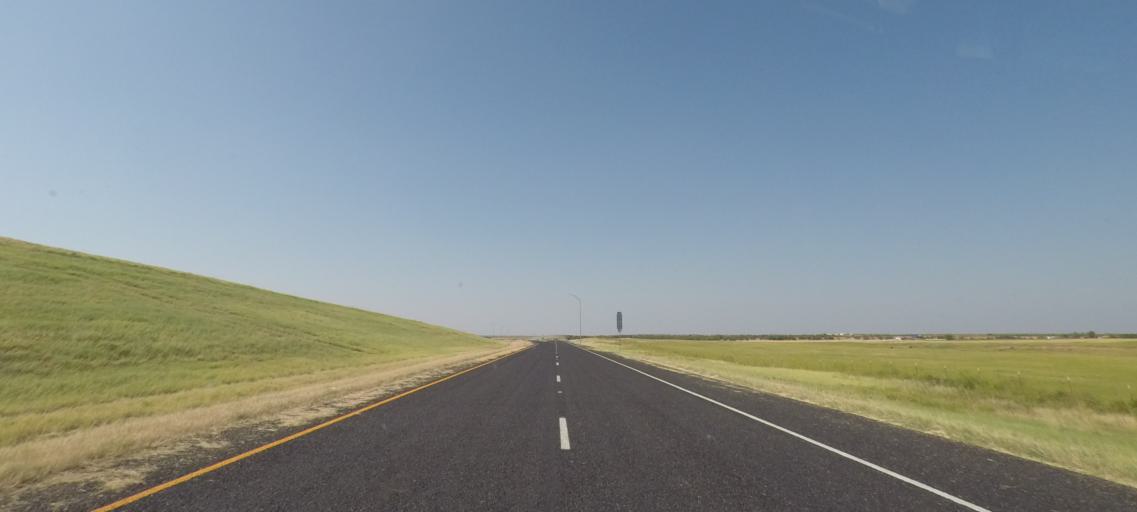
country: US
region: Texas
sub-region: Baylor County
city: Seymour
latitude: 33.5967
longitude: -99.2408
